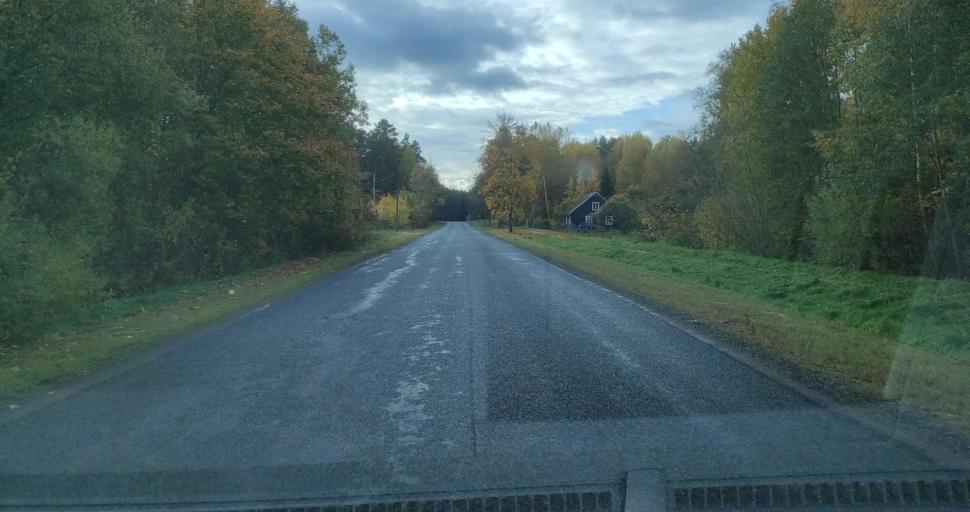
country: LV
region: Skrunda
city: Skrunda
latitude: 56.6652
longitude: 22.0231
